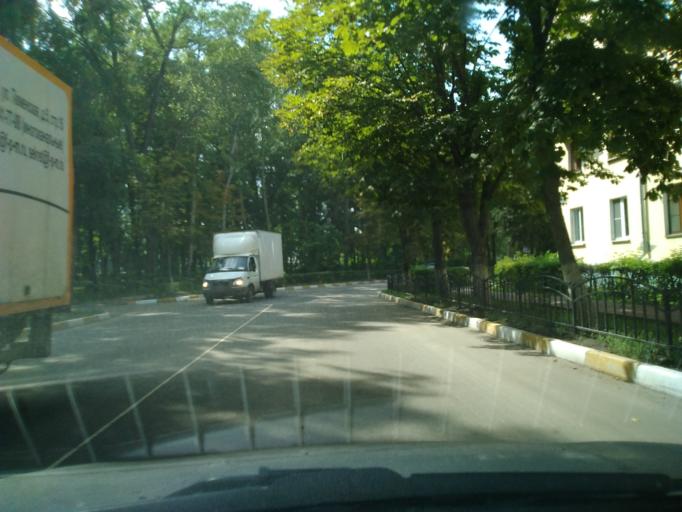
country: RU
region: Moskovskaya
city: Voskresensk
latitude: 55.3234
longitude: 38.6721
